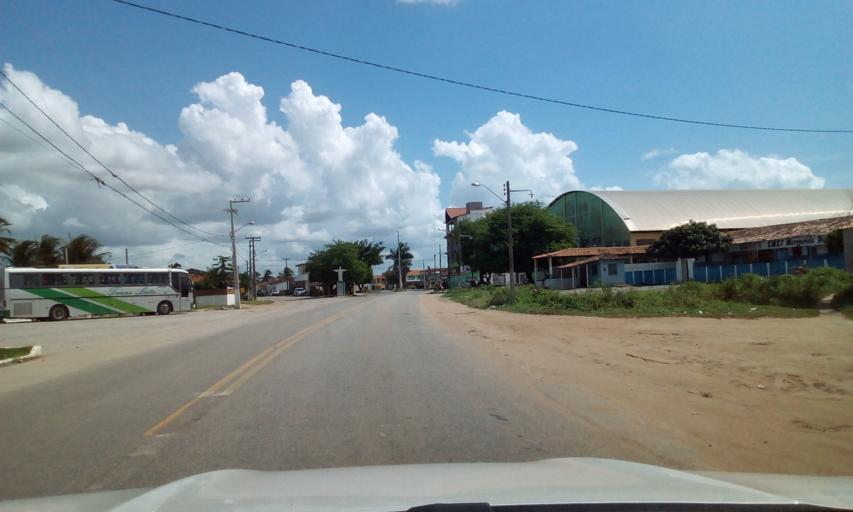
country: BR
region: Paraiba
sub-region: Guarabira
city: Guarabira
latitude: -6.8503
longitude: -35.3744
